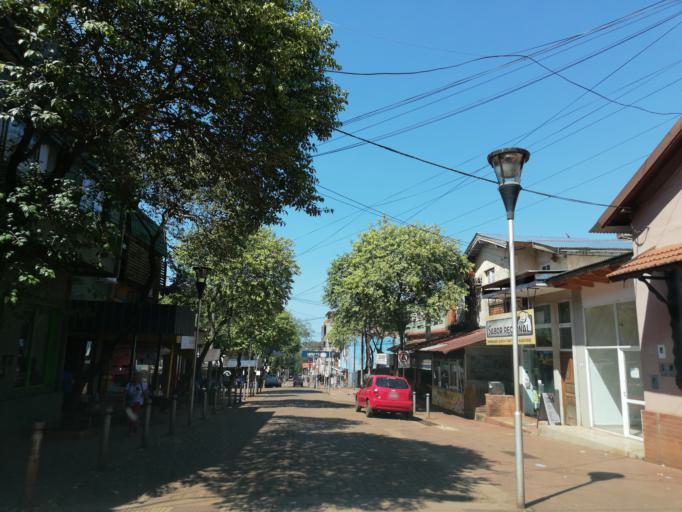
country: AR
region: Misiones
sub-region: Departamento de Eldorado
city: Eldorado
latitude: -26.4089
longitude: -54.6063
